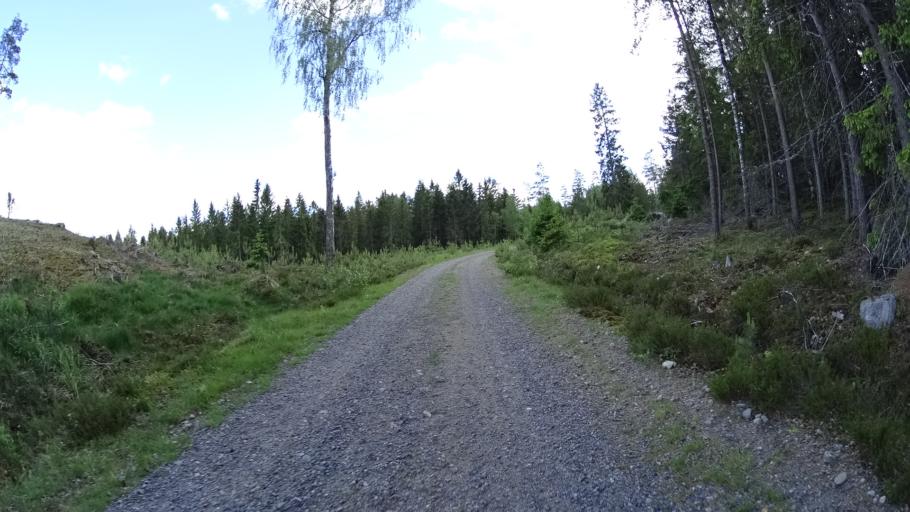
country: FI
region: Varsinais-Suomi
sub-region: Salo
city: Kisko
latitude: 60.1907
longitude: 23.5538
